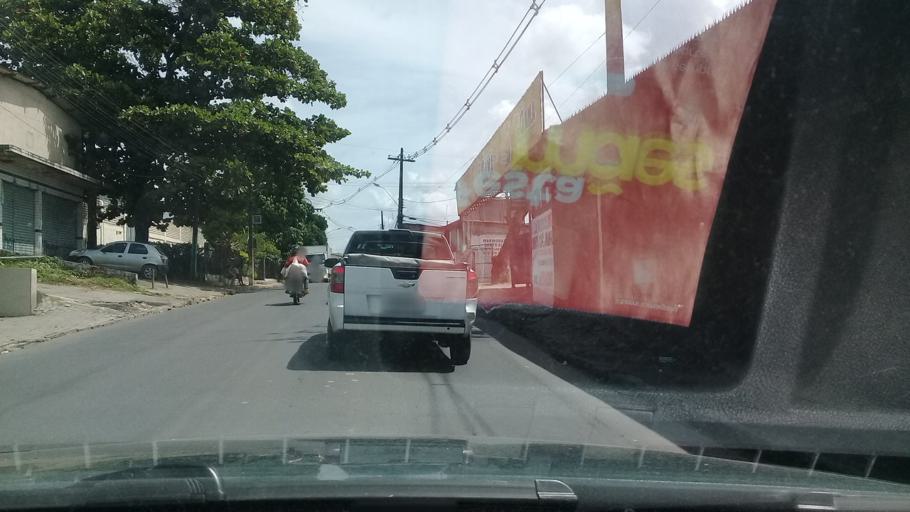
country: BR
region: Pernambuco
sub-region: Jaboatao Dos Guararapes
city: Jaboatao dos Guararapes
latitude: -8.0940
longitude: -35.0219
